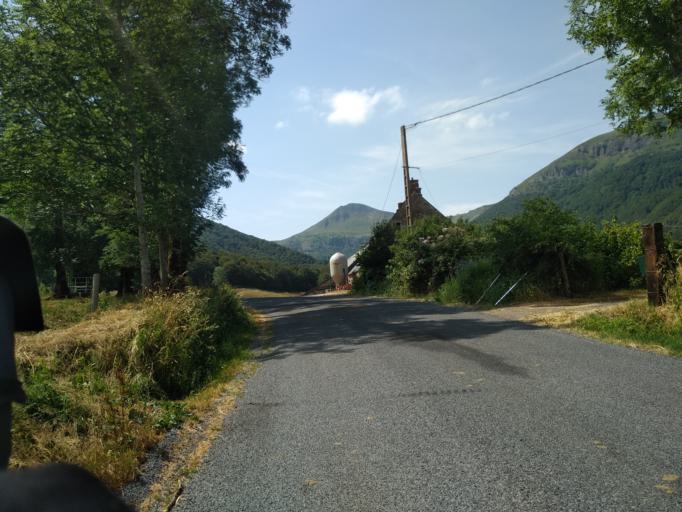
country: FR
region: Auvergne
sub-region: Departement du Cantal
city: Riom-es-Montagnes
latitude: 45.1357
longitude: 2.6975
